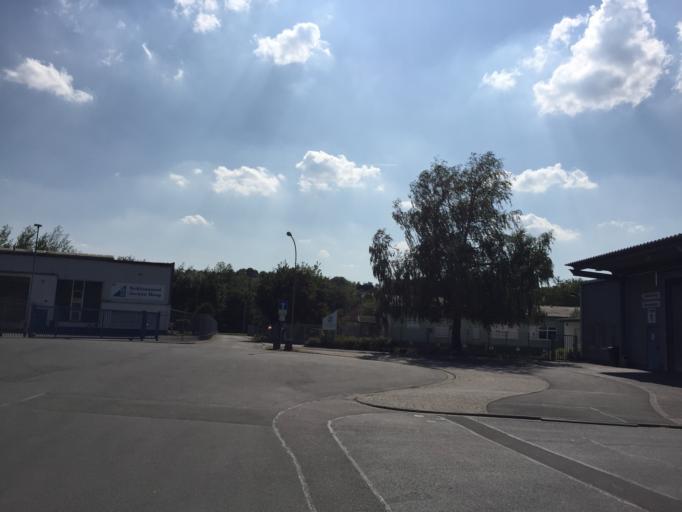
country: DE
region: Hesse
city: Solms
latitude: 50.5422
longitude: 8.4149
